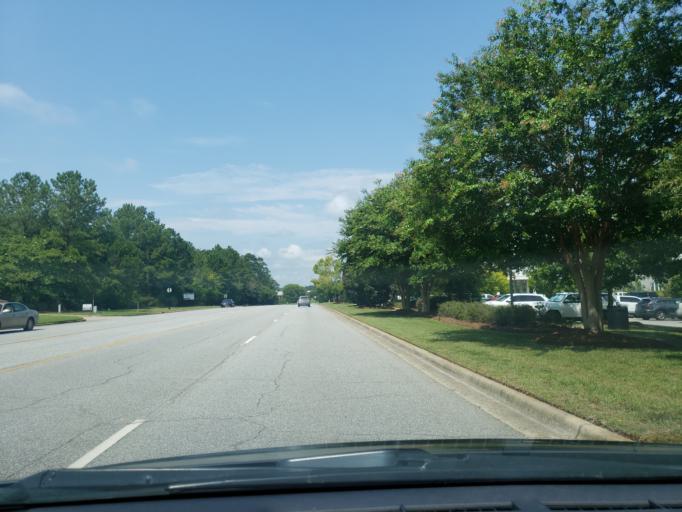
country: US
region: Georgia
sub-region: Dougherty County
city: Albany
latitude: 31.6092
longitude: -84.2156
